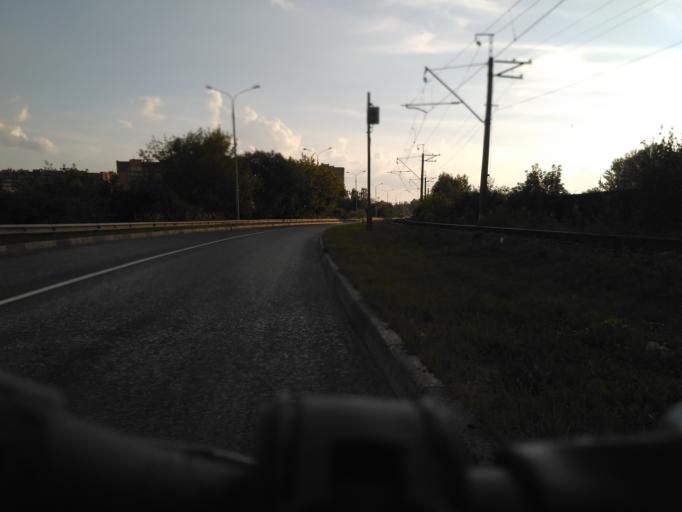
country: RU
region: Moskovskaya
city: Dubna
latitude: 56.7382
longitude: 37.1566
